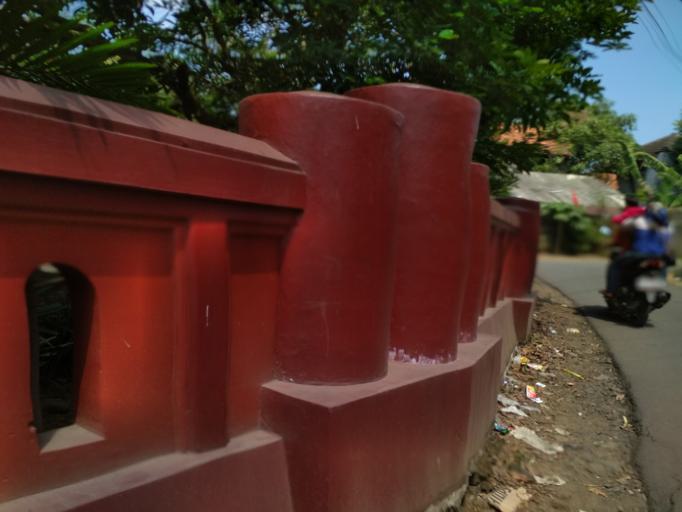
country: ID
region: West Java
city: Ciampea
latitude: -6.5637
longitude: 106.7457
